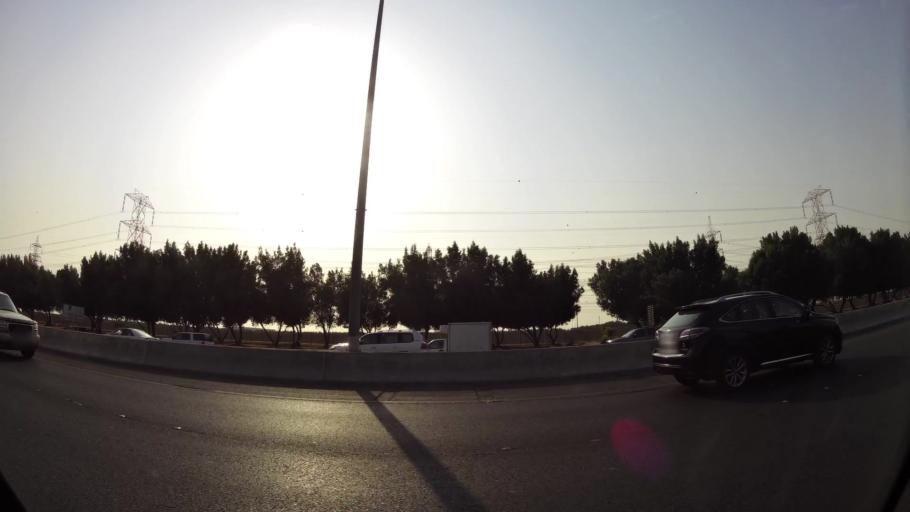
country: KW
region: Mubarak al Kabir
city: Sabah as Salim
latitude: 29.2474
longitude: 48.0478
